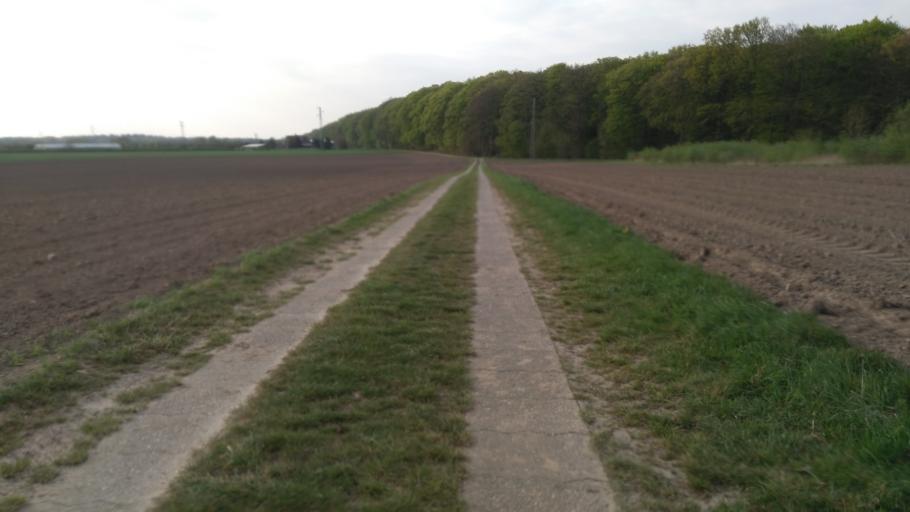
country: DE
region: Lower Saxony
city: Apensen
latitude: 53.4629
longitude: 9.6423
